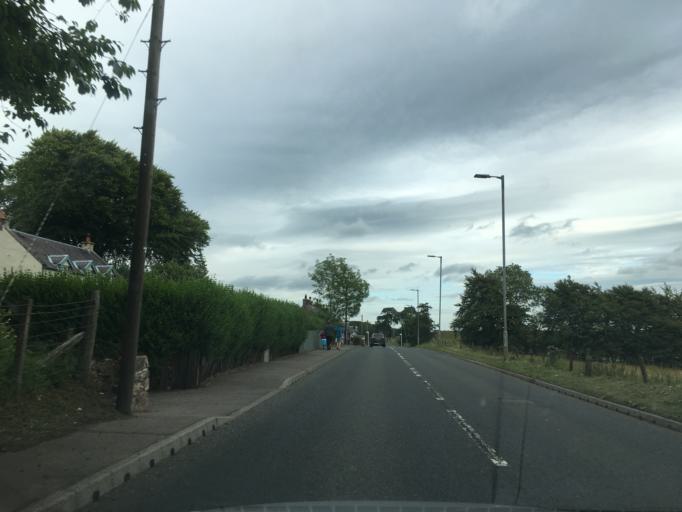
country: GB
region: Scotland
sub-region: The Scottish Borders
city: West Linton
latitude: 55.7042
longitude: -3.4275
